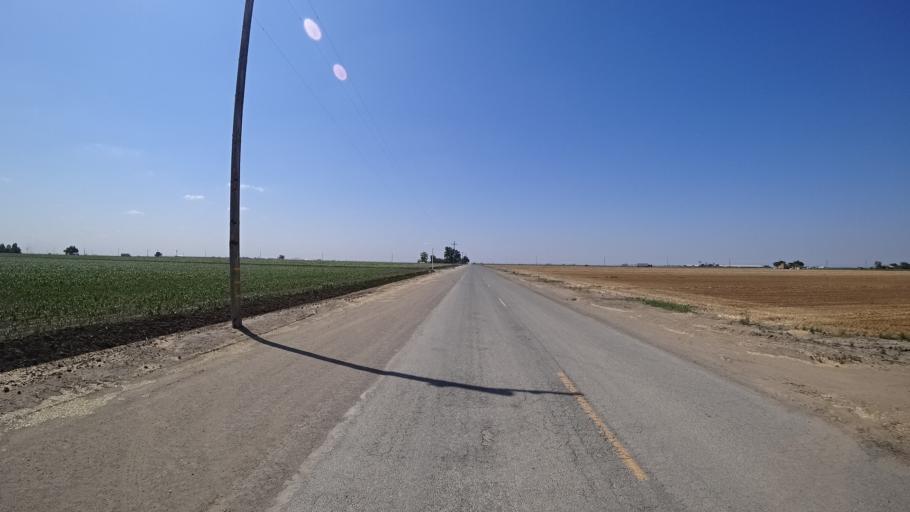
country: US
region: California
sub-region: Kings County
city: Home Garden
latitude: 36.2148
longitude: -119.6279
